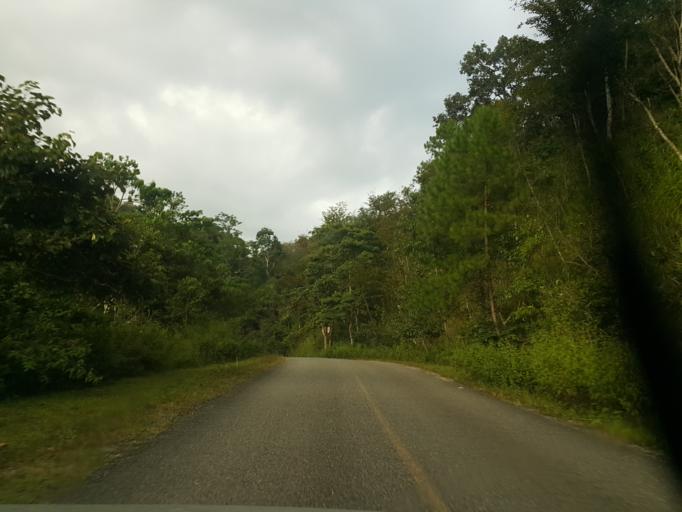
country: TH
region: Mae Hong Son
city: Khun Yuam
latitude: 18.7636
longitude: 98.1859
